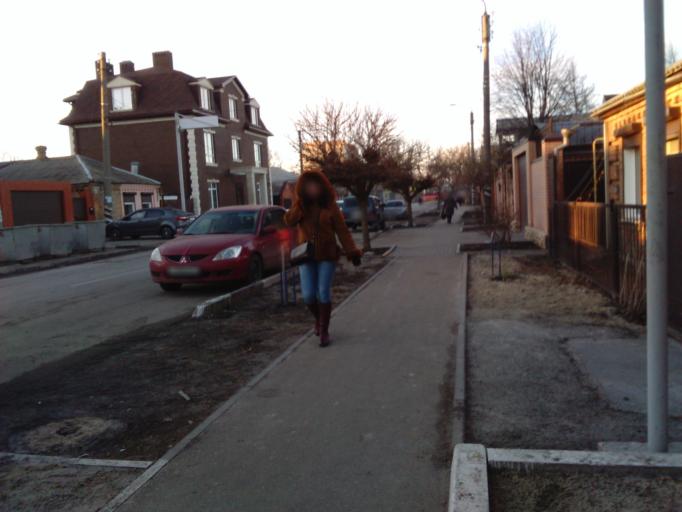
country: RU
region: Rostov
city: Bataysk
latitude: 47.1406
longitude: 39.7449
